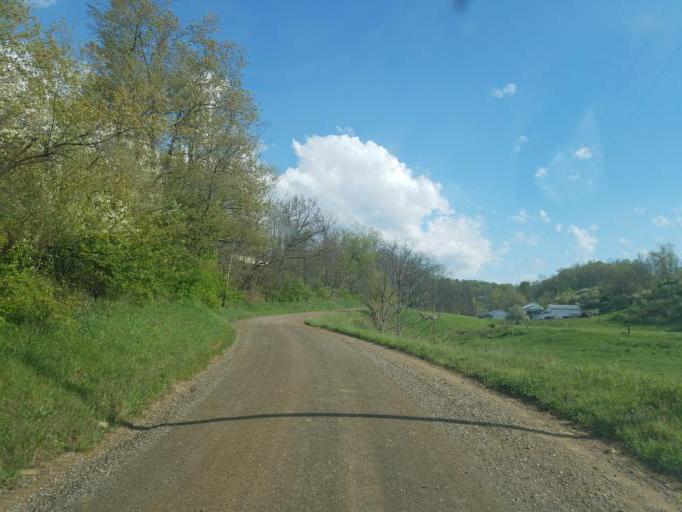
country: US
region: Ohio
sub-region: Knox County
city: Oak Hill
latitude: 40.4111
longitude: -82.2213
